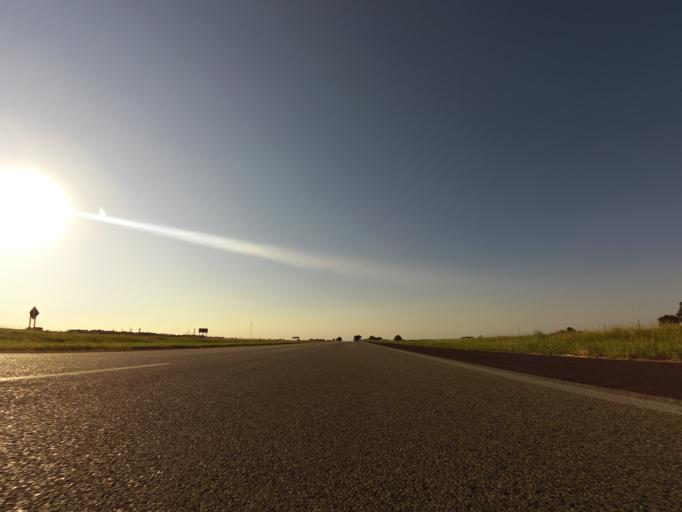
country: US
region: Kansas
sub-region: Reno County
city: Haven
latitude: 37.8997
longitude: -97.7932
